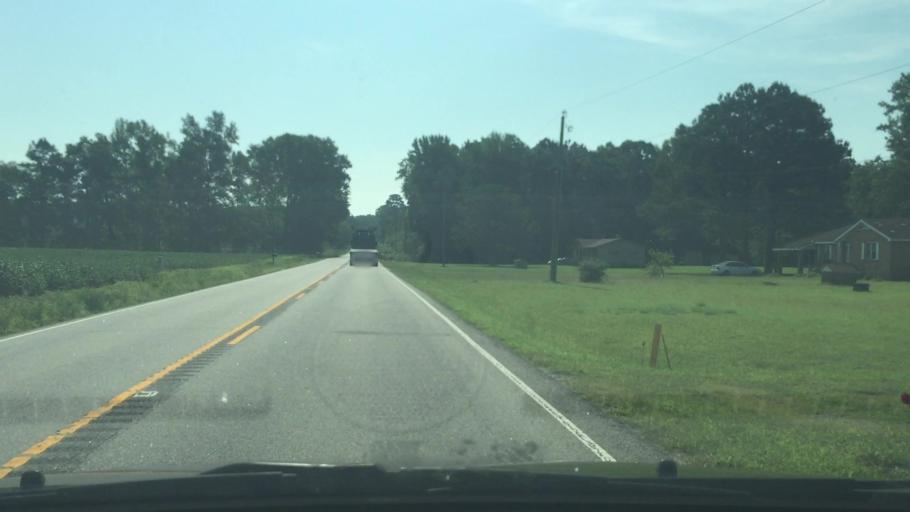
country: US
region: Virginia
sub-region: Sussex County
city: Sussex
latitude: 36.9766
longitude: -77.2110
